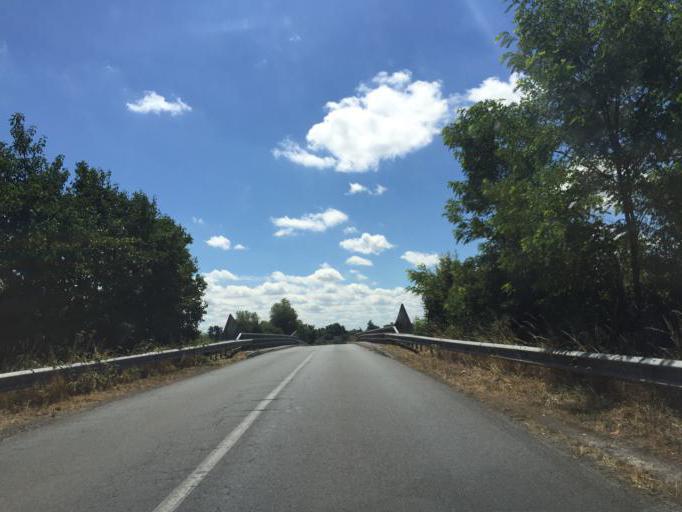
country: FR
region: Auvergne
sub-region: Departement de l'Allier
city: Moulins
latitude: 46.5917
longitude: 3.3321
